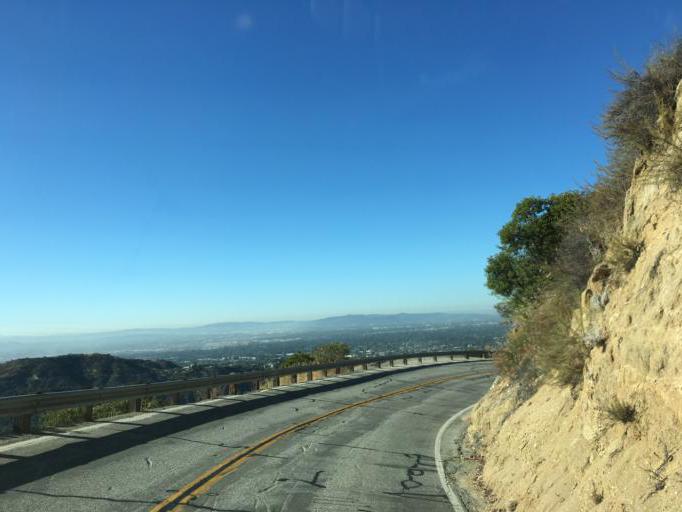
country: US
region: California
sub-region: Los Angeles County
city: Sierra Madre
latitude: 34.1768
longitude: -118.0294
